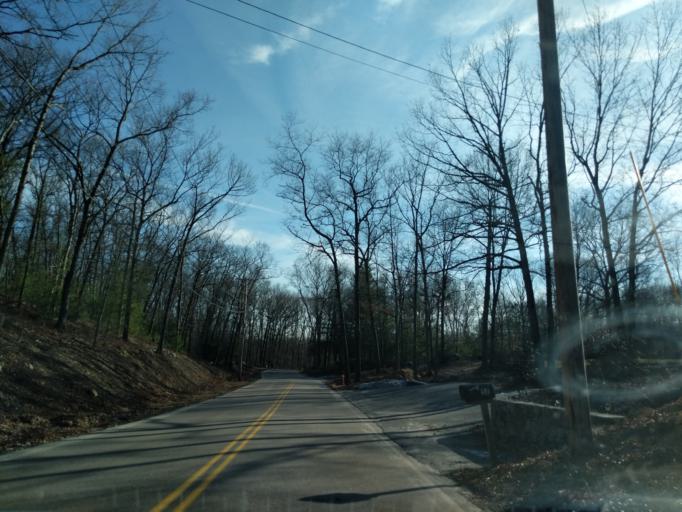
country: US
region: Massachusetts
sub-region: Norfolk County
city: Bellingham
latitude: 42.0511
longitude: -71.5066
